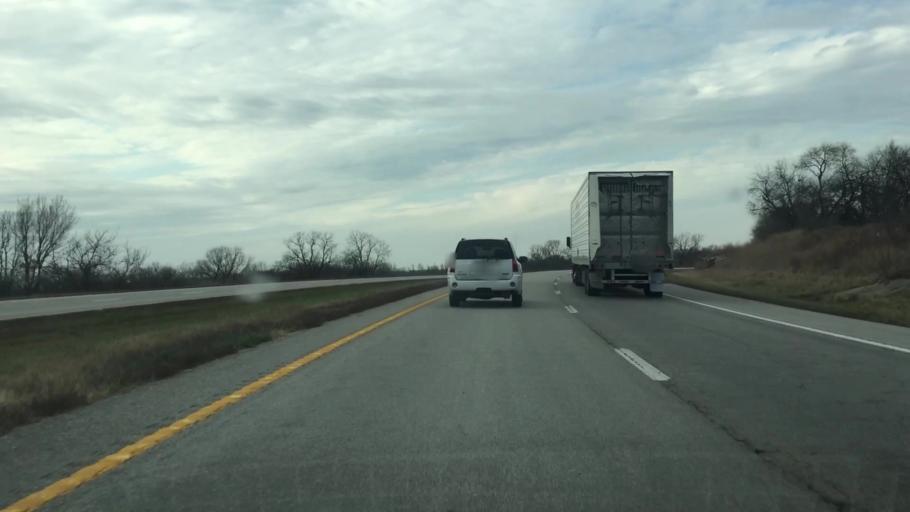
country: US
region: Missouri
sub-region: Cass County
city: Garden City
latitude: 38.5187
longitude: -94.1391
